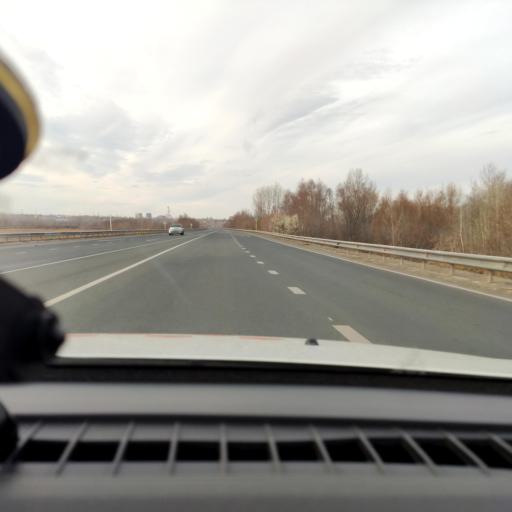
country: RU
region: Samara
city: Novokuybyshevsk
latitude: 53.1348
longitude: 49.9674
